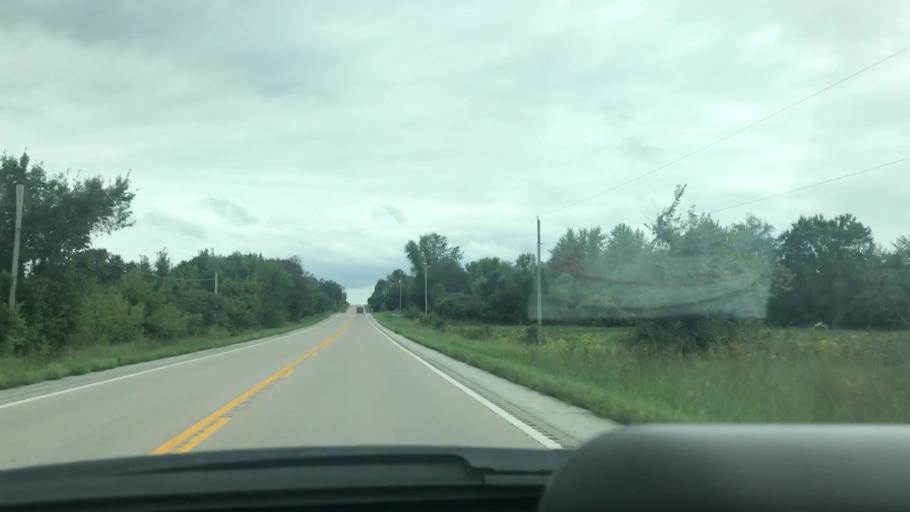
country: US
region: Missouri
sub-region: Dallas County
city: Buffalo
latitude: 37.6973
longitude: -93.1044
